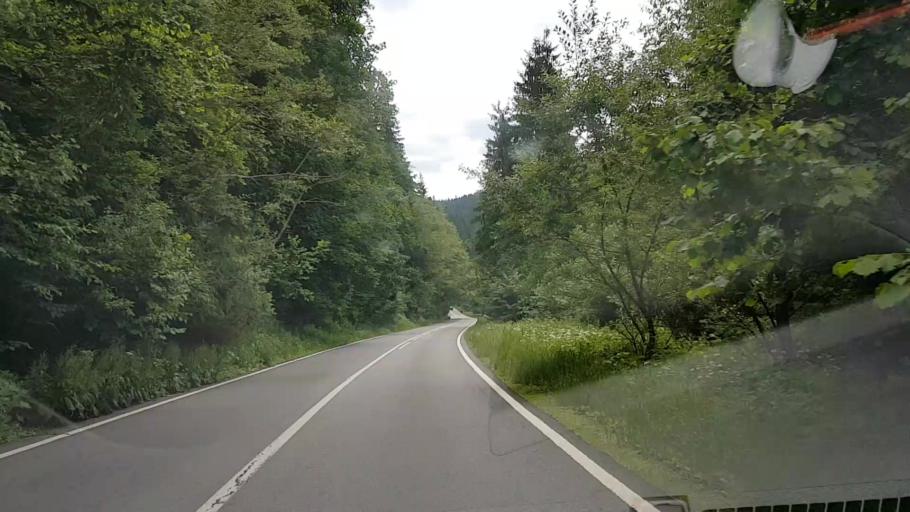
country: RO
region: Suceava
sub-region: Comuna Crucea
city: Crucea
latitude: 47.3691
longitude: 25.5897
